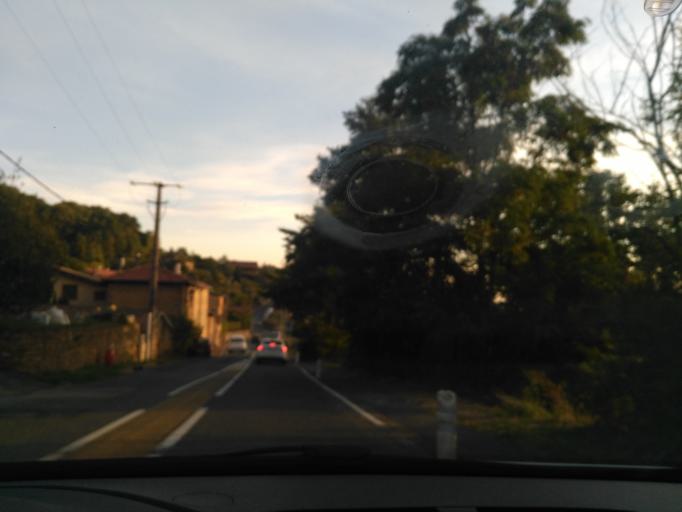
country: FR
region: Rhone-Alpes
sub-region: Departement du Rhone
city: Limonest
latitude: 45.8510
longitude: 4.7955
